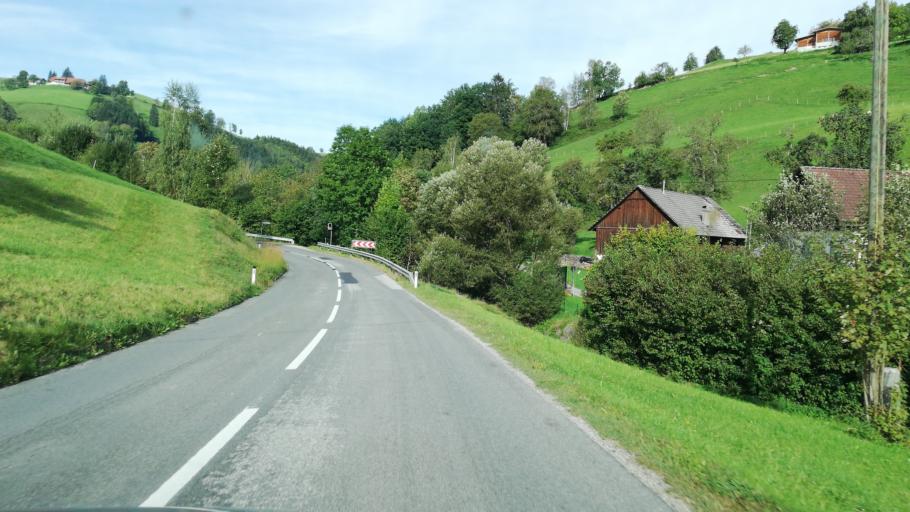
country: AT
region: Upper Austria
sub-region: Politischer Bezirk Steyr-Land
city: Maria Neustift
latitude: 47.9737
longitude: 14.5681
